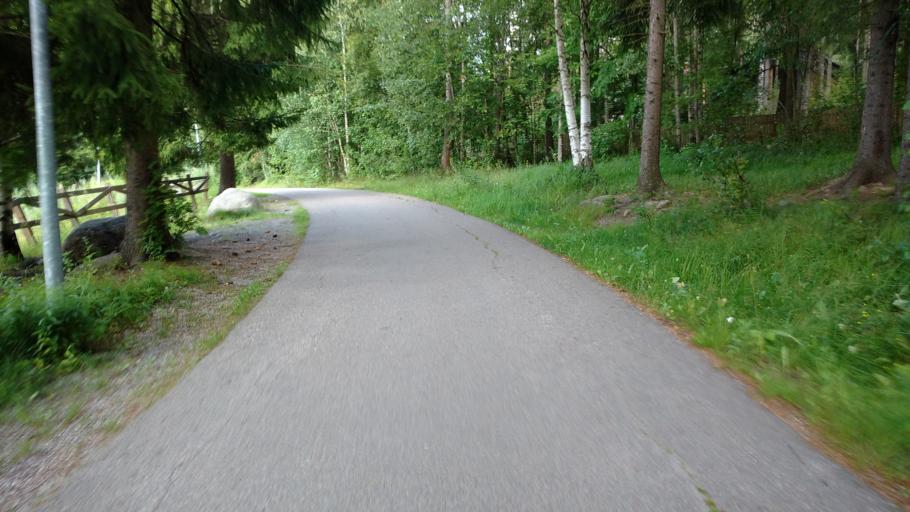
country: FI
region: Varsinais-Suomi
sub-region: Salo
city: Salo
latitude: 60.4038
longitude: 23.1747
